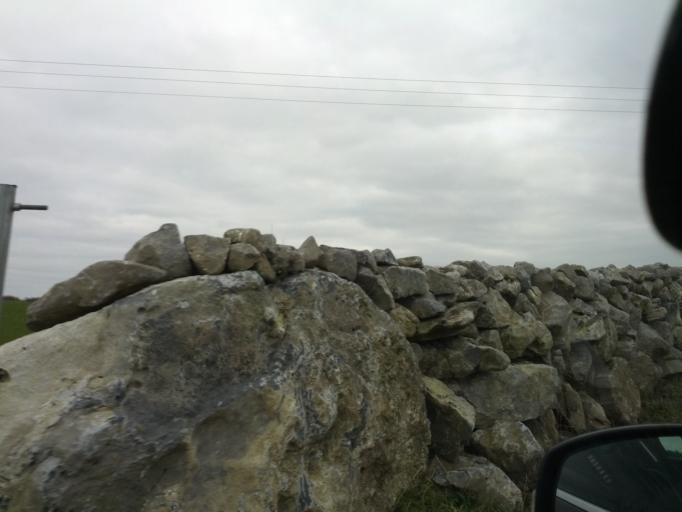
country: IE
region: Connaught
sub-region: County Galway
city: Oranmore
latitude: 53.2168
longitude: -8.8902
